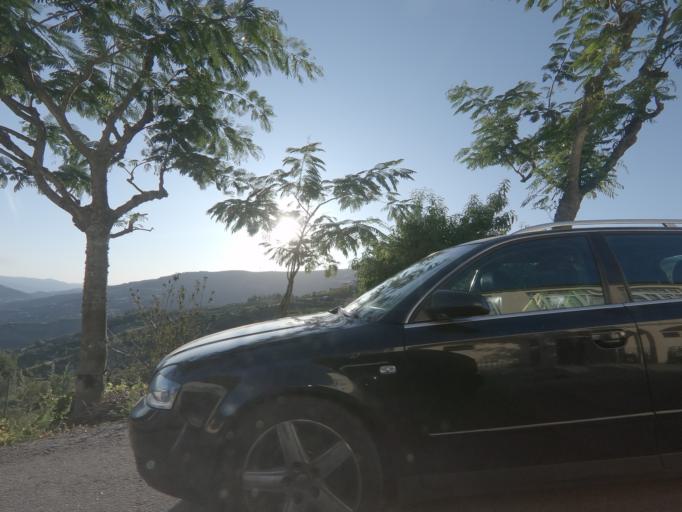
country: PT
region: Vila Real
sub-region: Santa Marta de Penaguiao
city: Santa Marta de Penaguiao
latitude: 41.1936
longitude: -7.8249
